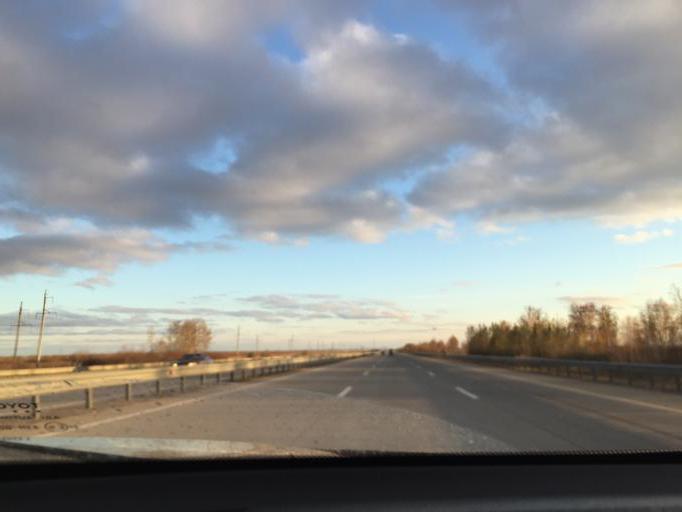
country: KZ
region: Astana Qalasy
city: Astana
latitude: 51.3290
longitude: 71.3447
